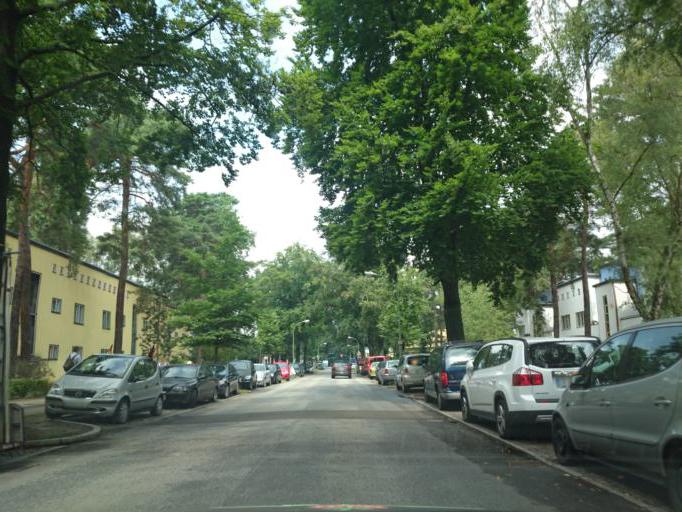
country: DE
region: Berlin
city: Zehlendorf Bezirk
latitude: 52.4489
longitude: 13.2559
